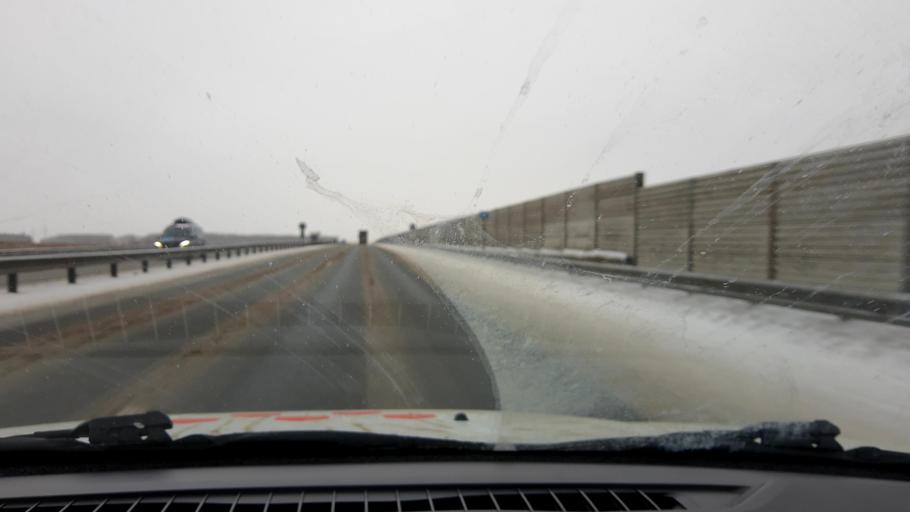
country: RU
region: Nizjnij Novgorod
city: Burevestnik
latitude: 56.1096
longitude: 43.9771
